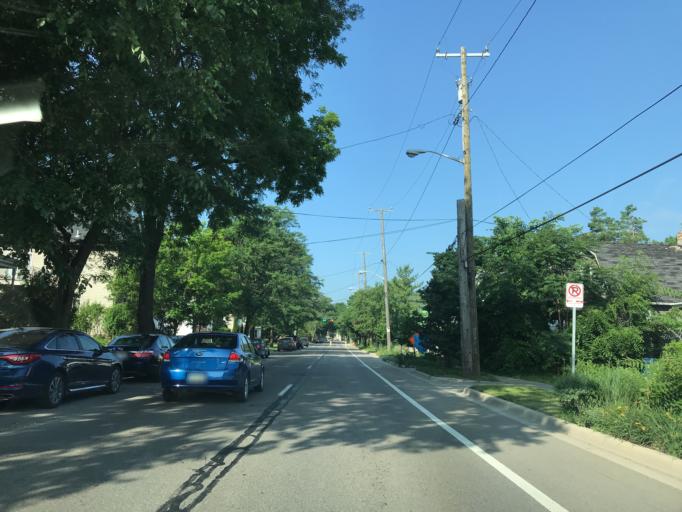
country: US
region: Michigan
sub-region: Washtenaw County
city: Ann Arbor
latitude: 42.2867
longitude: -83.7443
